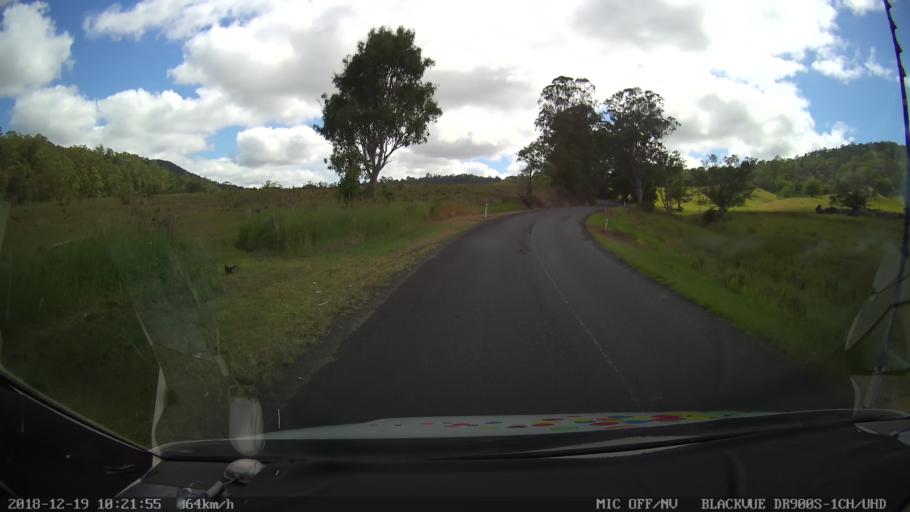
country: AU
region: New South Wales
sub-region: Kyogle
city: Kyogle
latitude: -28.5953
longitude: 153.0635
